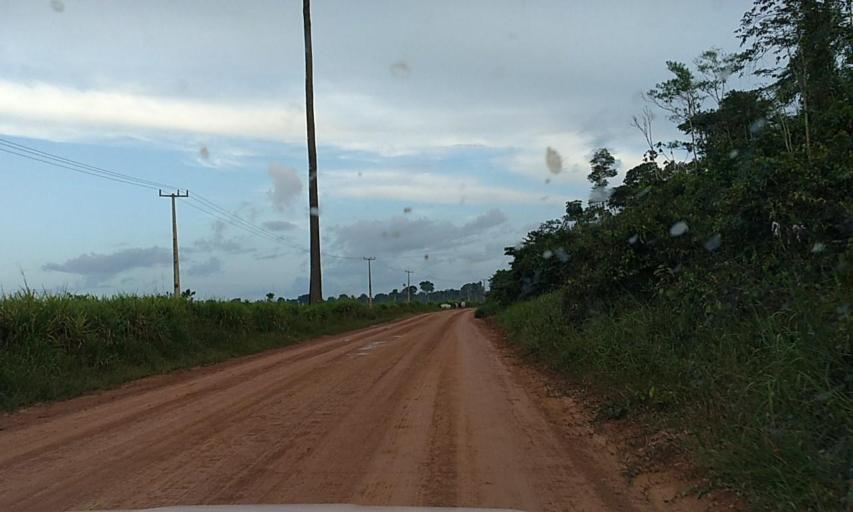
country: BR
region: Para
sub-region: Senador Jose Porfirio
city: Senador Jose Porfirio
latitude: -2.7035
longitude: -51.8153
